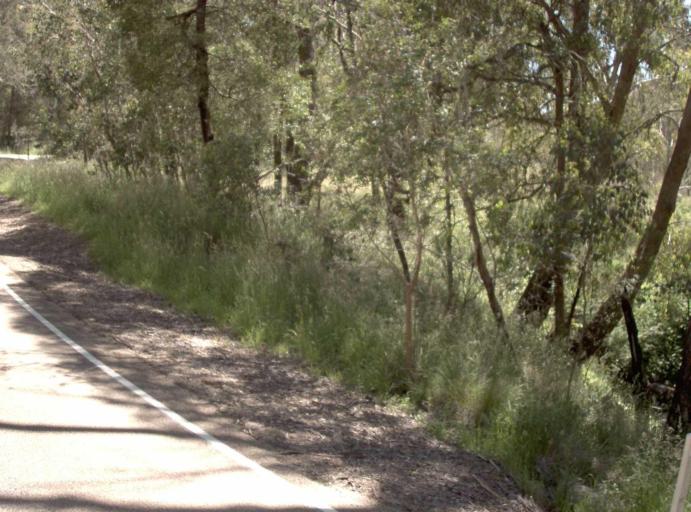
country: AU
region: Victoria
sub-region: East Gippsland
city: Lakes Entrance
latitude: -37.2371
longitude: 148.2585
